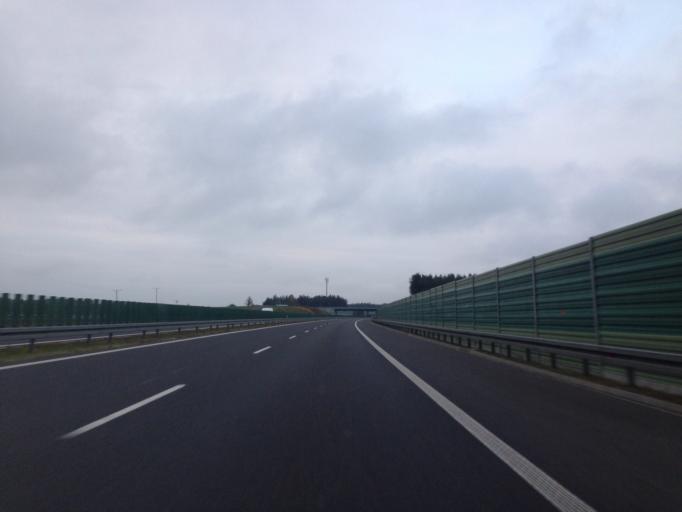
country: PL
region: Kujawsko-Pomorskie
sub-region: Powiat swiecki
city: Warlubie
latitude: 53.6384
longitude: 18.6422
